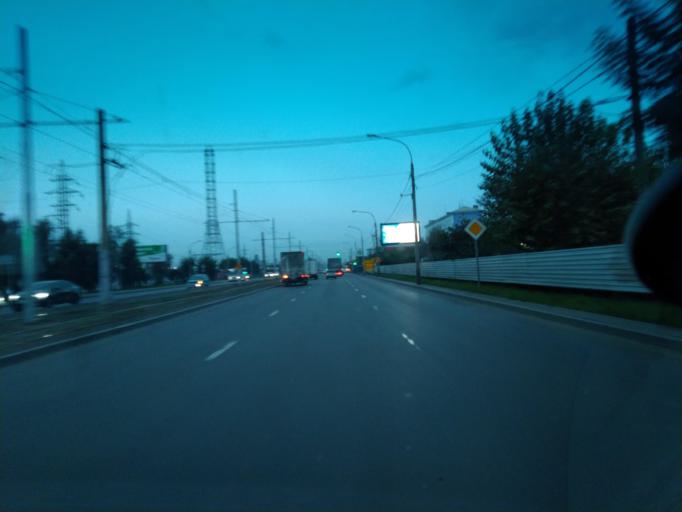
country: RU
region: Krasnoyarskiy
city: Berezovka
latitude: 56.0228
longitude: 93.0141
